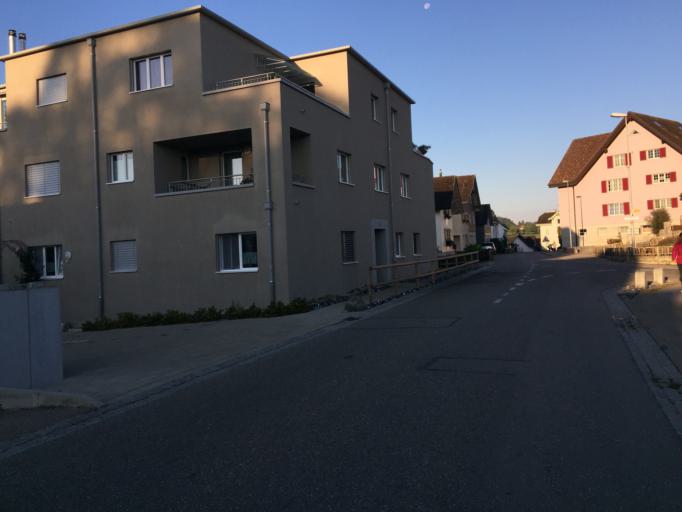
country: CH
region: Saint Gallen
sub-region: Wahlkreis Wil
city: Oberuzwil
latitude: 47.4204
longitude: 9.1385
